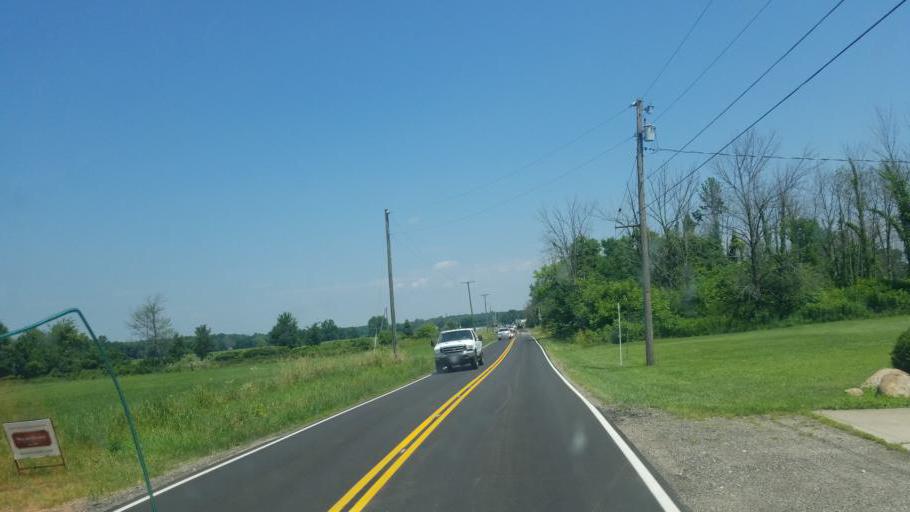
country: US
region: Ohio
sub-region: Richland County
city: Ontario
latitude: 40.8078
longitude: -82.6285
